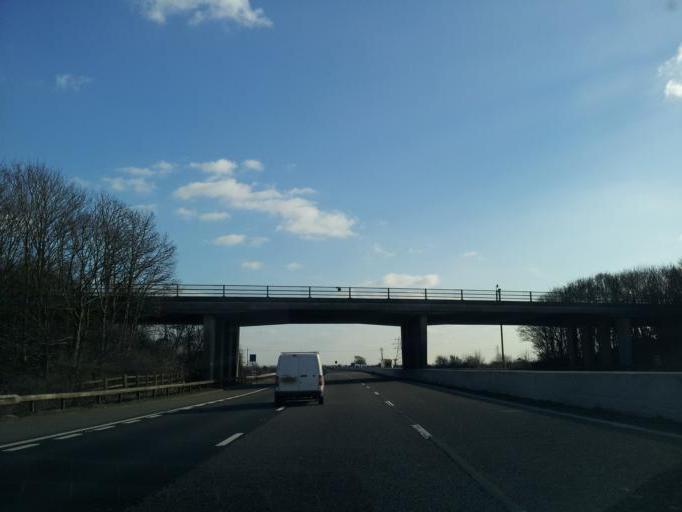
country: GB
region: England
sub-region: North Somerset
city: Bleadon
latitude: 51.2638
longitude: -2.9221
